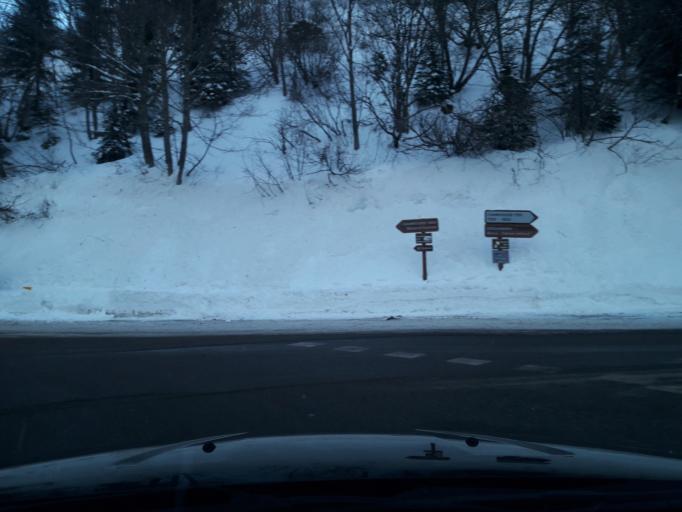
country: FR
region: Rhone-Alpes
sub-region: Departement de l'Isere
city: Livet-et-Gavet
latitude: 45.1234
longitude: 5.8780
